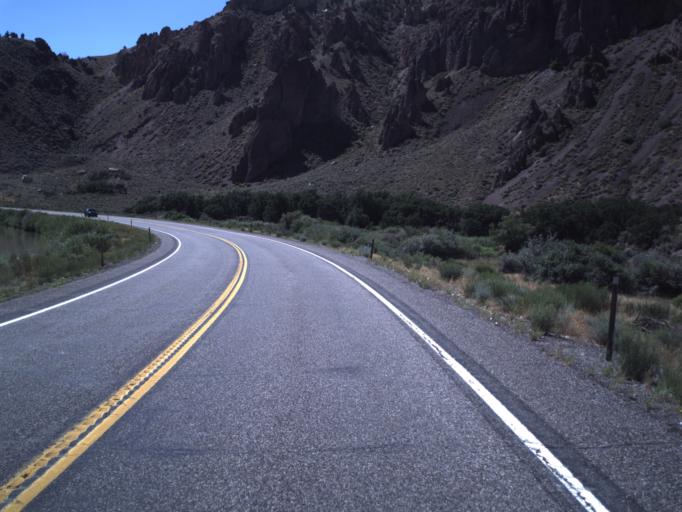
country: US
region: Utah
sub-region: Sevier County
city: Monroe
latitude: 38.4985
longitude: -112.2570
